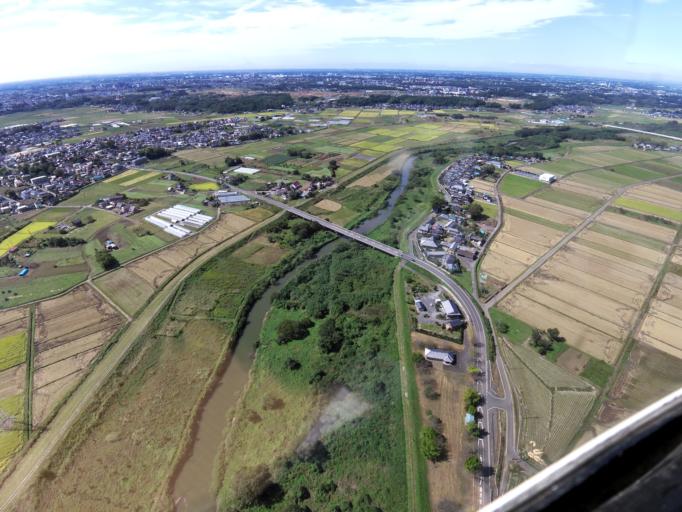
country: JP
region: Ibaraki
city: Naka
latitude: 36.1144
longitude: 140.1486
